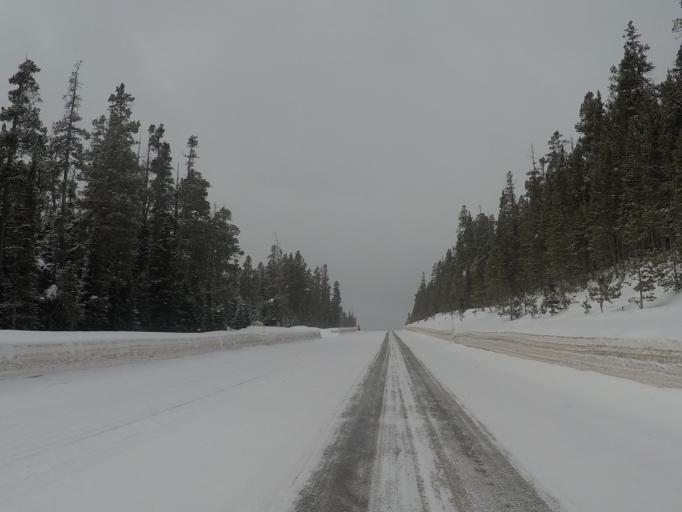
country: US
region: Montana
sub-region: Meagher County
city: White Sulphur Springs
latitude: 46.8437
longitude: -110.6932
